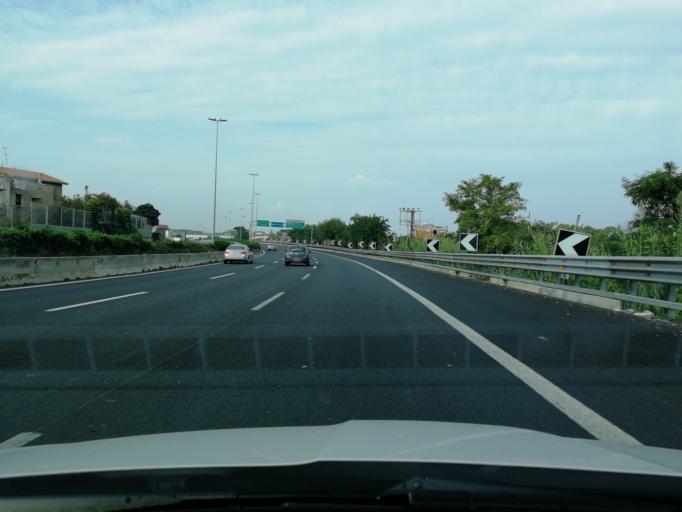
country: IT
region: Latium
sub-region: Citta metropolitana di Roma Capitale
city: Setteville
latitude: 41.9144
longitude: 12.6158
